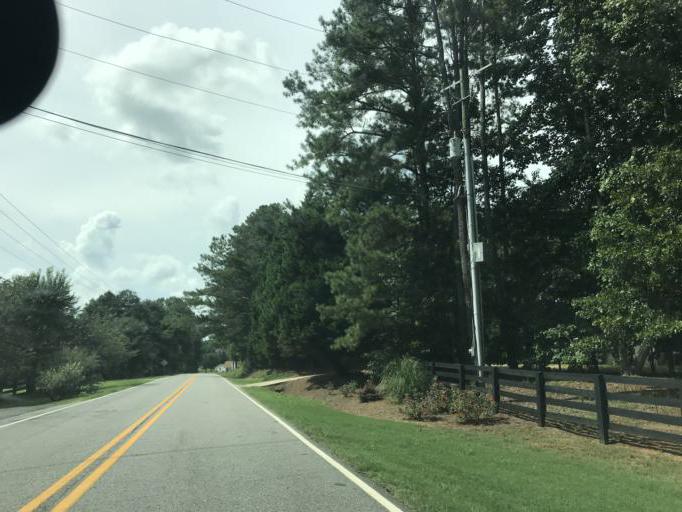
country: US
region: Georgia
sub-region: Forsyth County
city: Cumming
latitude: 34.2240
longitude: -84.2417
